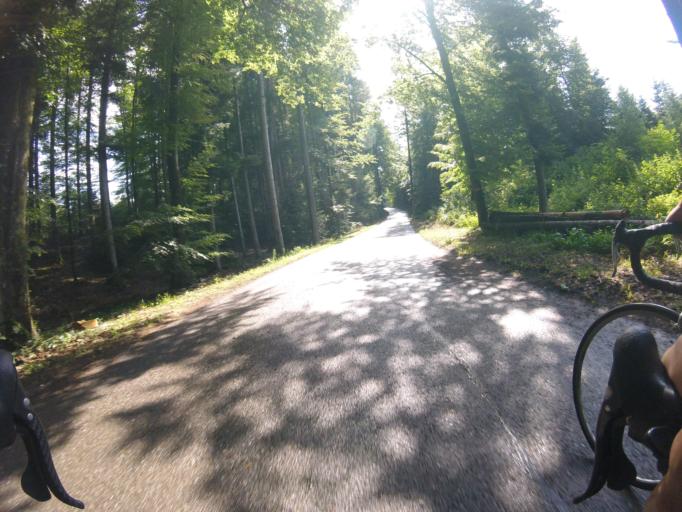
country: CH
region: Bern
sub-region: Bern-Mittelland District
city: Stettlen
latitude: 46.9394
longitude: 7.5217
